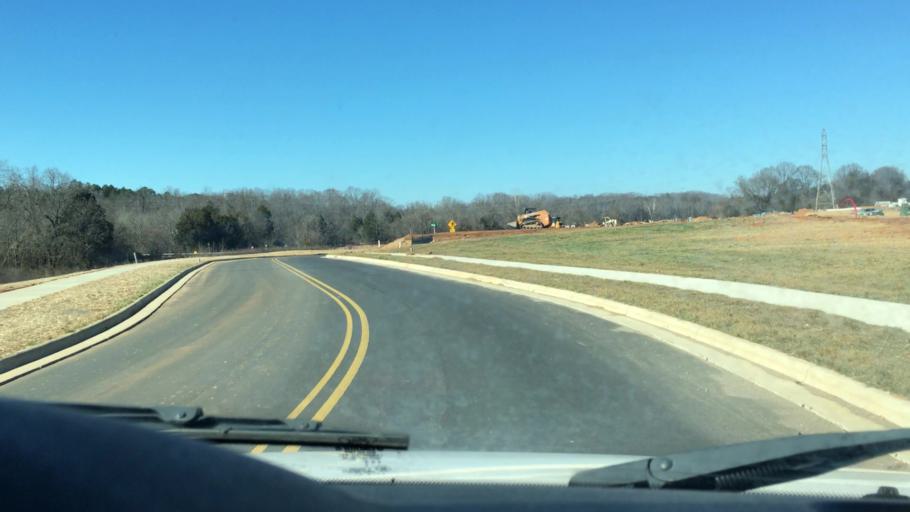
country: US
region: North Carolina
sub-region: Gaston County
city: Davidson
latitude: 35.4746
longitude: -80.8215
